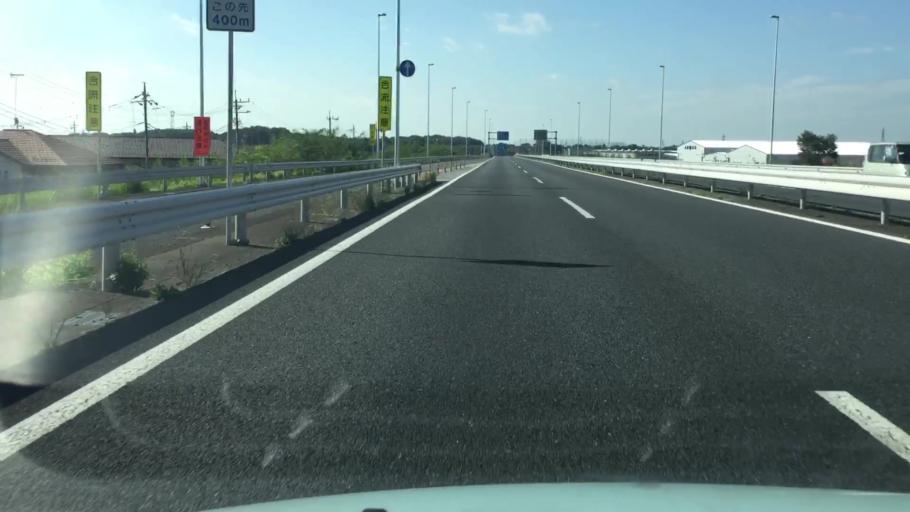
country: JP
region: Tochigi
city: Mooka
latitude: 36.4548
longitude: 139.9780
